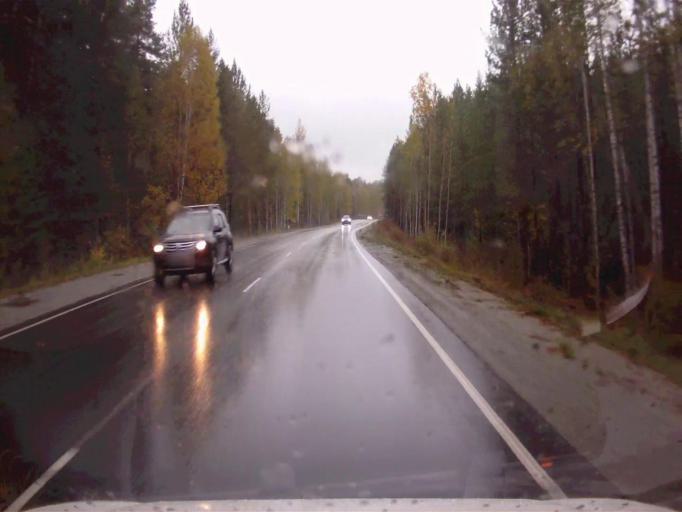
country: RU
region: Chelyabinsk
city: Kyshtym
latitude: 55.6530
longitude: 60.5768
